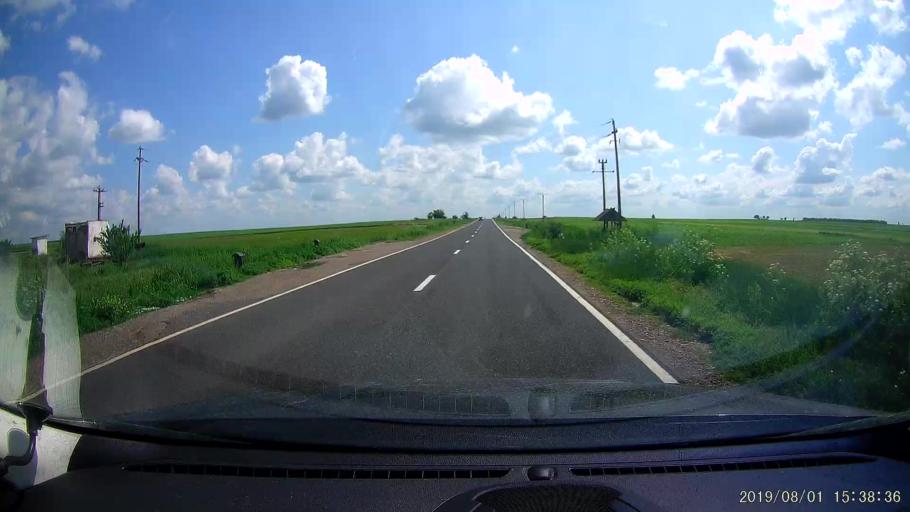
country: RO
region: Braila
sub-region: Comuna Insuratei
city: Insuratei
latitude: 44.8775
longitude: 27.5735
